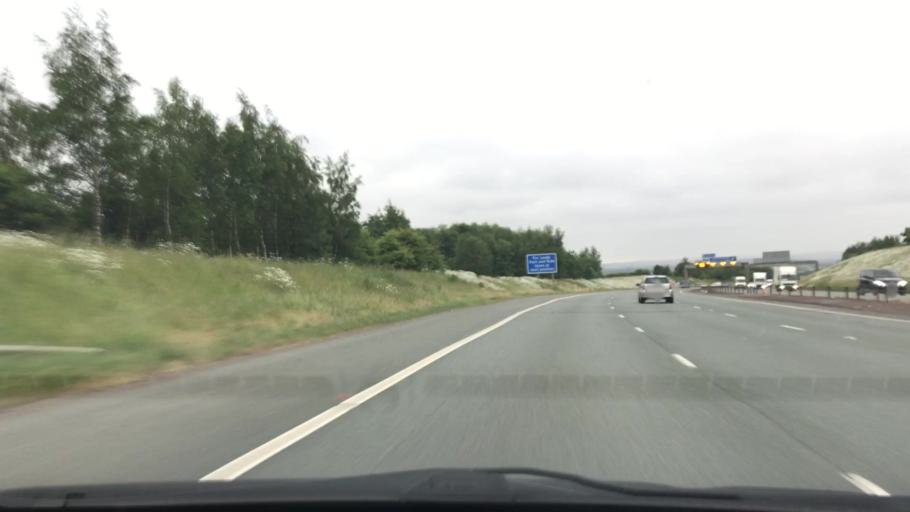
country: GB
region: England
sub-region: City and Borough of Leeds
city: Swillington
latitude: 53.7741
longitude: -1.4408
